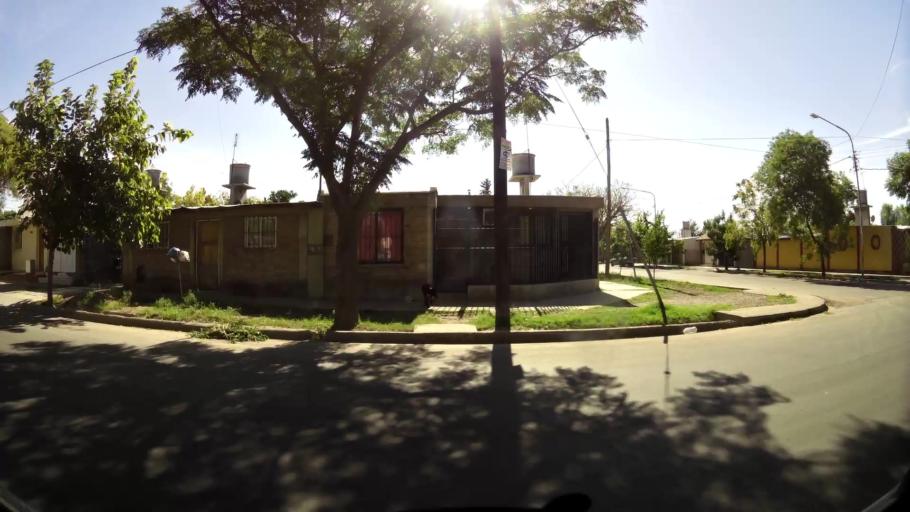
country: AR
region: Mendoza
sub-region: Departamento de Godoy Cruz
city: Godoy Cruz
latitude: -32.9436
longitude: -68.8103
